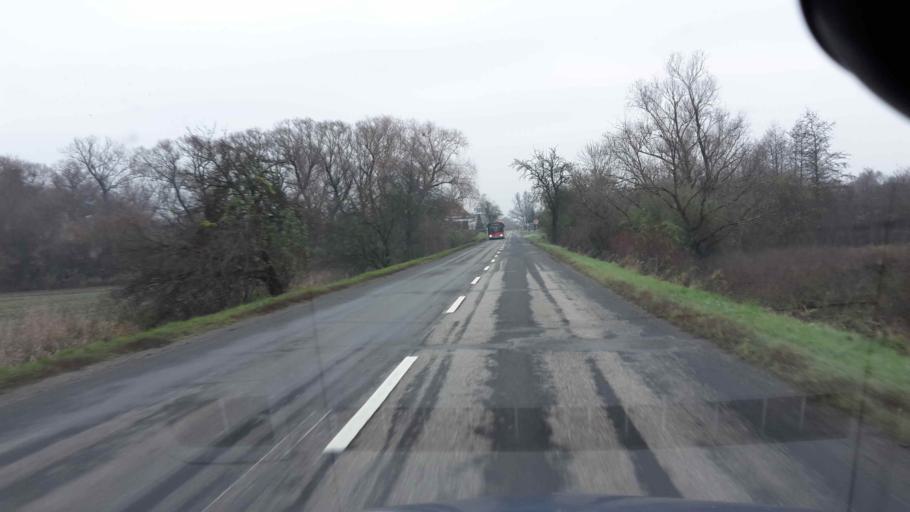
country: CZ
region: Olomoucky
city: Horka nad Moravou
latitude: 49.6081
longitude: 17.2107
